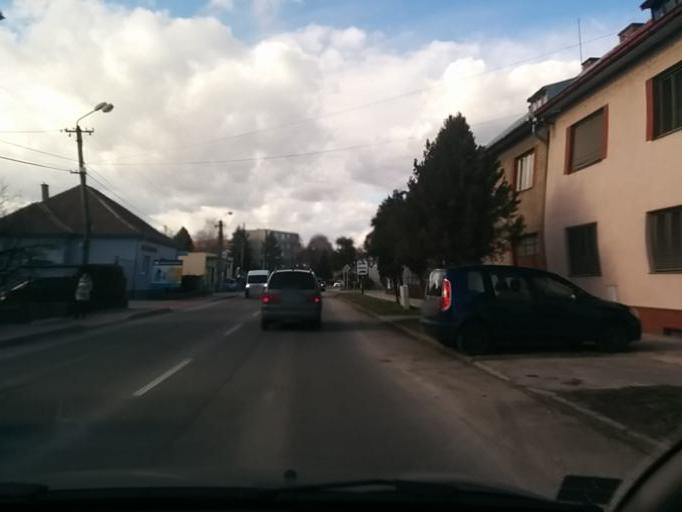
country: SK
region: Trenciansky
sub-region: Okres Nove Mesto nad Vahom
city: Nove Mesto nad Vahom
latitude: 48.7614
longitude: 17.8347
